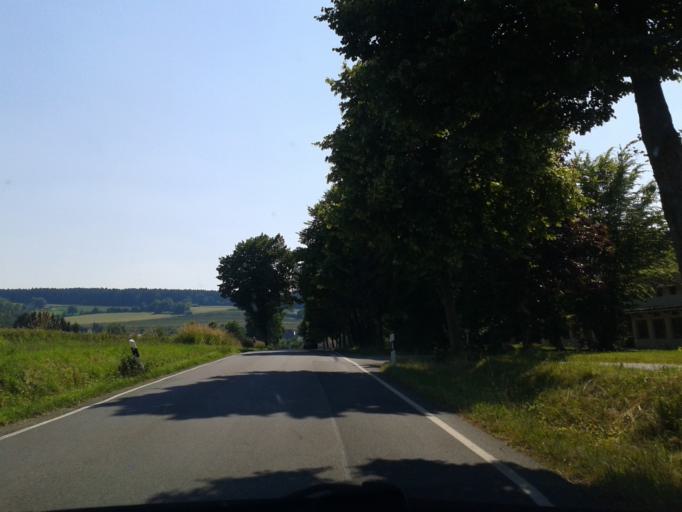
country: DE
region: North Rhine-Westphalia
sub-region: Regierungsbezirk Detmold
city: Barntrup
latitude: 51.9854
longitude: 9.0868
